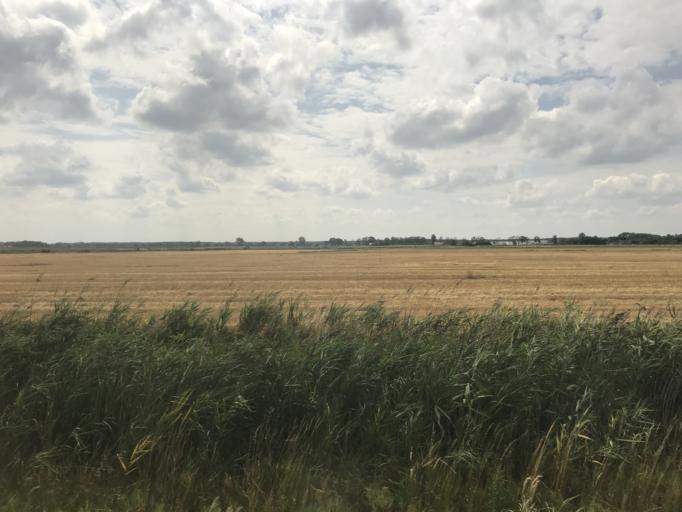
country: PL
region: Greater Poland Voivodeship
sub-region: Powiat poznanski
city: Pobiedziska
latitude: 52.4835
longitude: 17.3024
